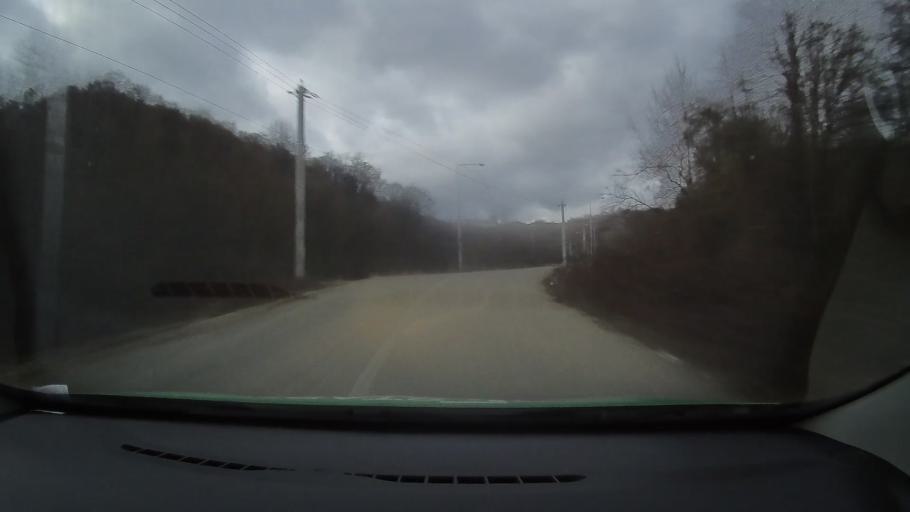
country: RO
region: Prahova
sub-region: Comuna Adunati
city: Adunati
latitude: 45.1259
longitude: 25.6116
